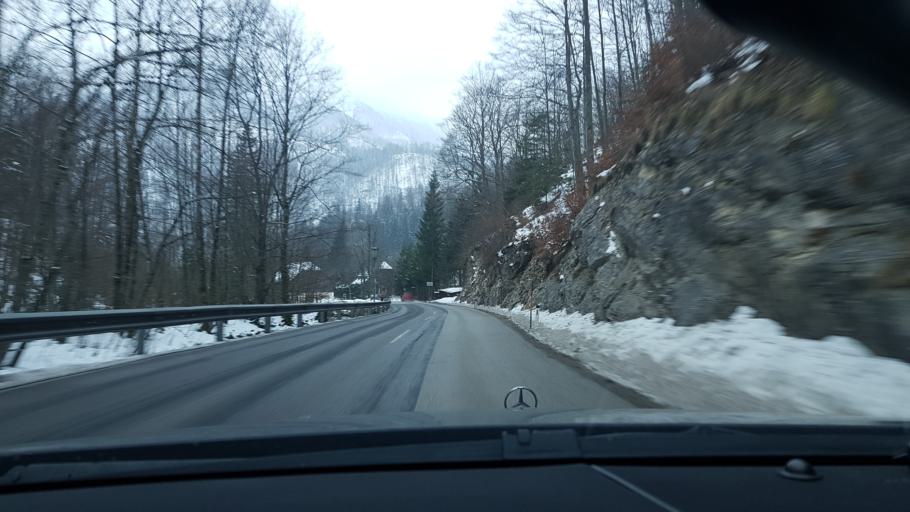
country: AT
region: Lower Austria
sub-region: Politischer Bezirk Scheibbs
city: Gaming
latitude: 47.8666
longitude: 15.1140
